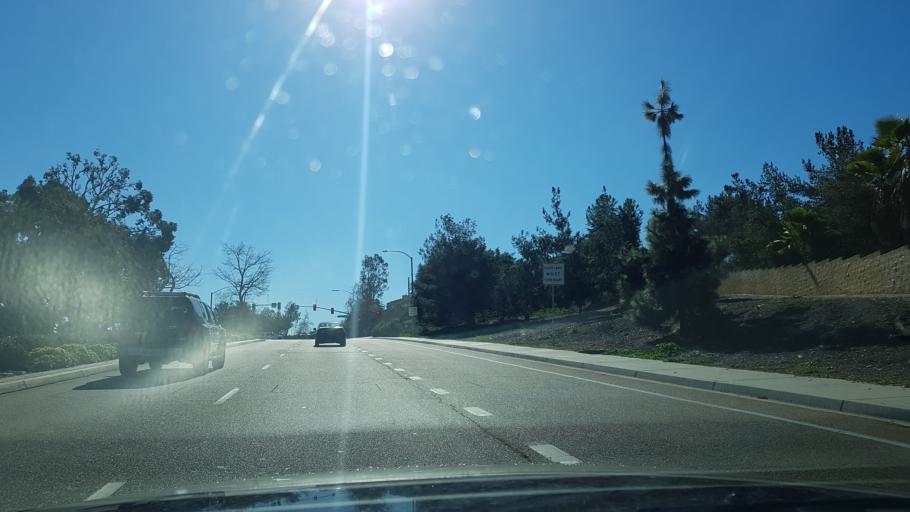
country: US
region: California
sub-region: San Diego County
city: Escondido
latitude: 33.1086
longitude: -117.1045
